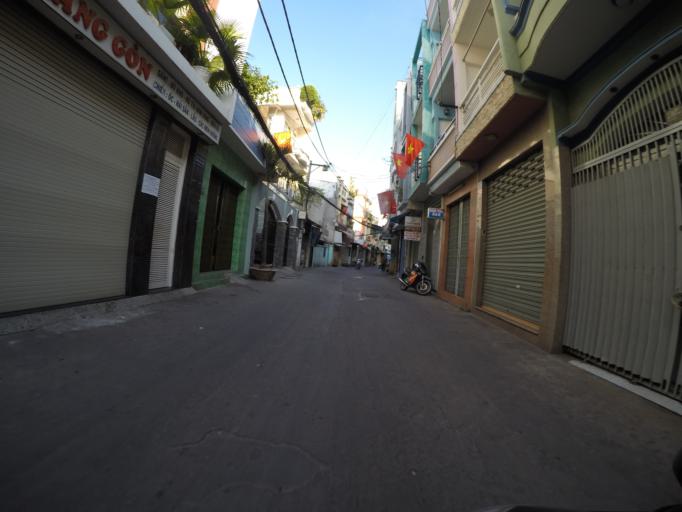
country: VN
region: Ho Chi Minh City
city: Quan Phu Nhuan
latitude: 10.7980
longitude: 106.6829
